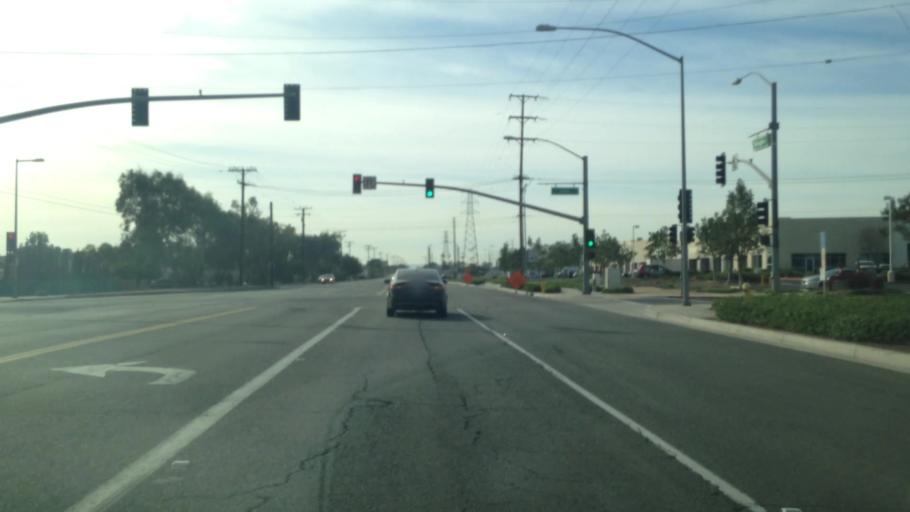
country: US
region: California
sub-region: Riverside County
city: Mira Loma
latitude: 34.0052
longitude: -117.5061
